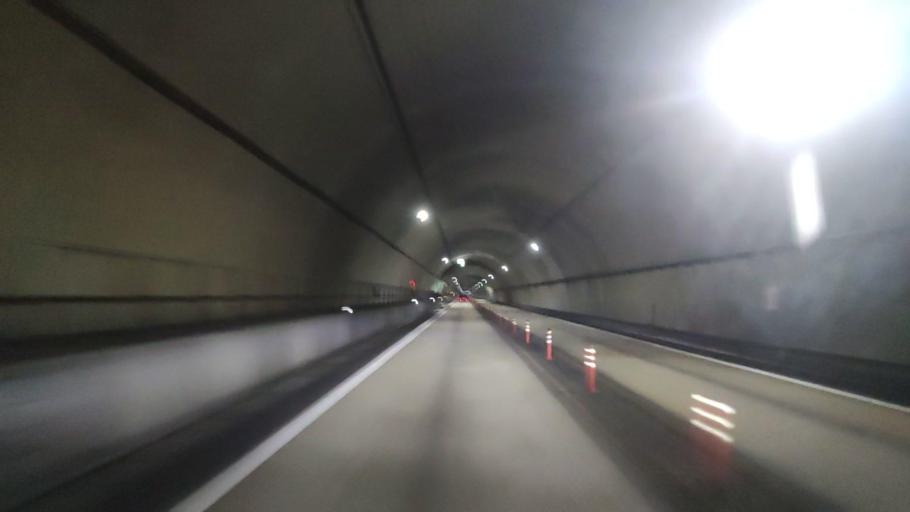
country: JP
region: Wakayama
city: Tanabe
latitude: 33.5451
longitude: 135.5230
